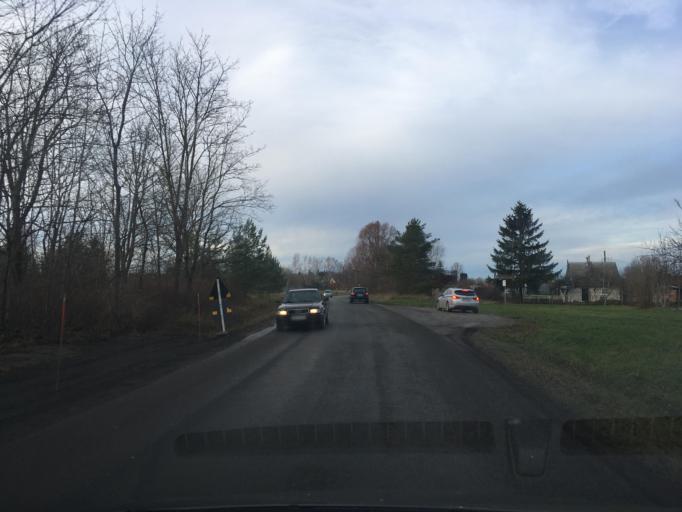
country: EE
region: Ida-Virumaa
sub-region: Sillamaee linn
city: Sillamae
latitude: 59.3840
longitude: 27.7558
